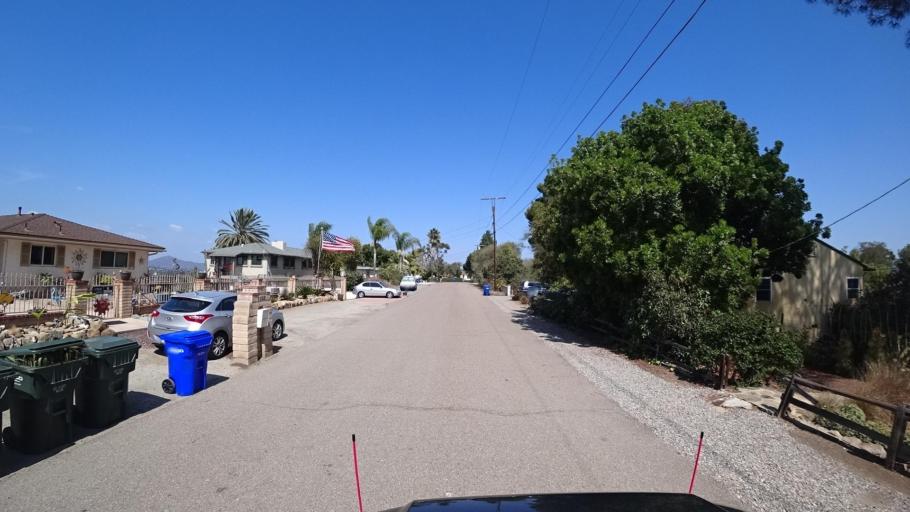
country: US
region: California
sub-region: San Diego County
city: Spring Valley
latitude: 32.7339
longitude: -116.9907
